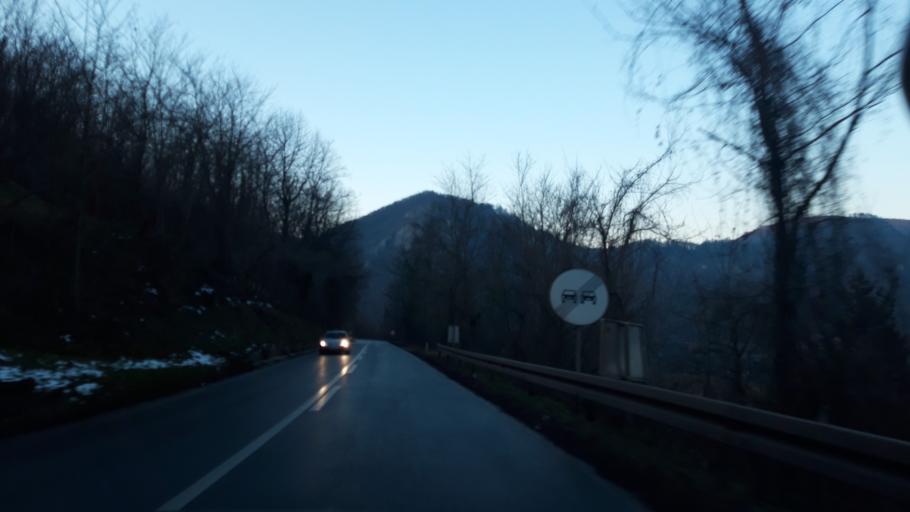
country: RS
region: Central Serbia
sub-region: Macvanski Okrug
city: Mali Zvornik
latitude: 44.3358
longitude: 19.1333
